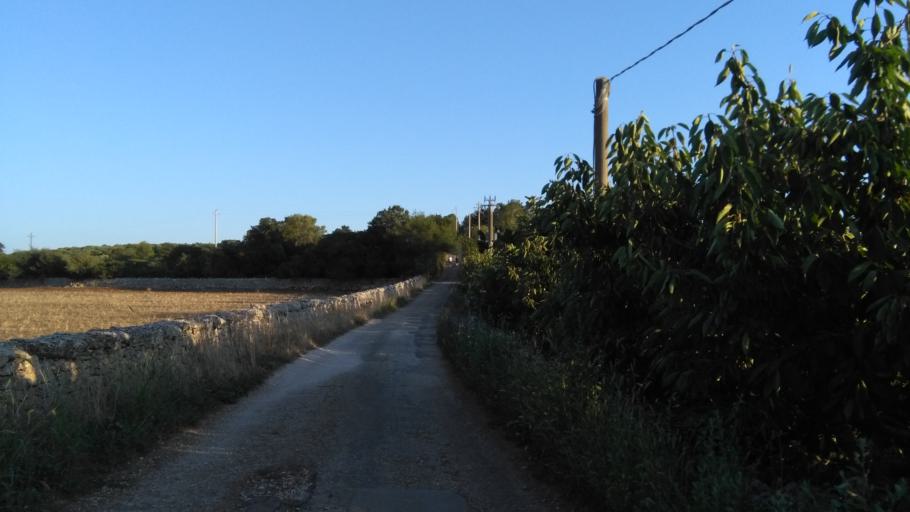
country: IT
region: Apulia
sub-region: Provincia di Bari
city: Putignano
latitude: 40.8298
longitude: 17.0765
